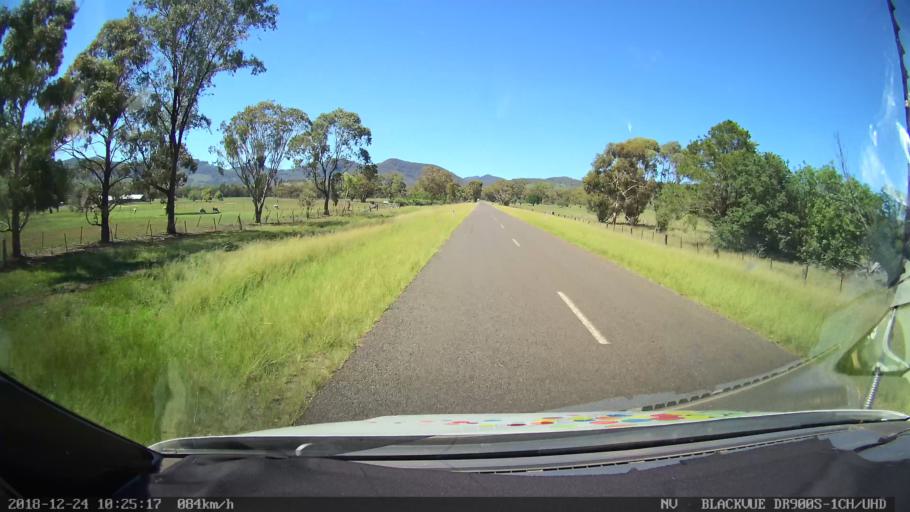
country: AU
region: New South Wales
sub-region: Liverpool Plains
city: Quirindi
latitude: -31.7969
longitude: 150.5292
